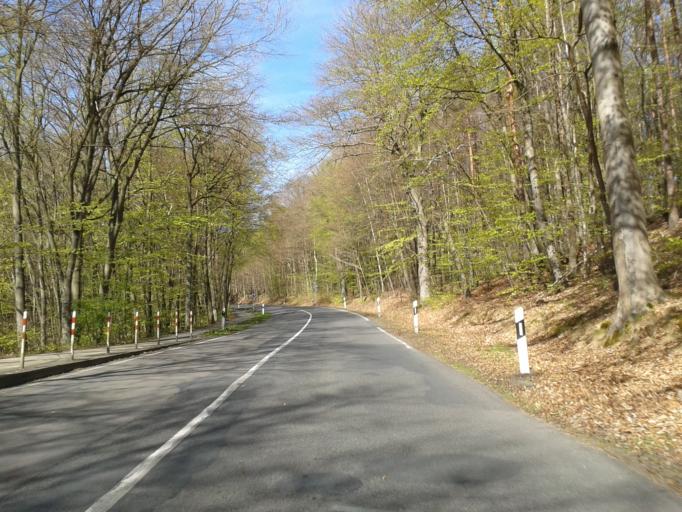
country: DE
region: Lower Saxony
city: Schnega
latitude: 52.9297
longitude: 10.9124
